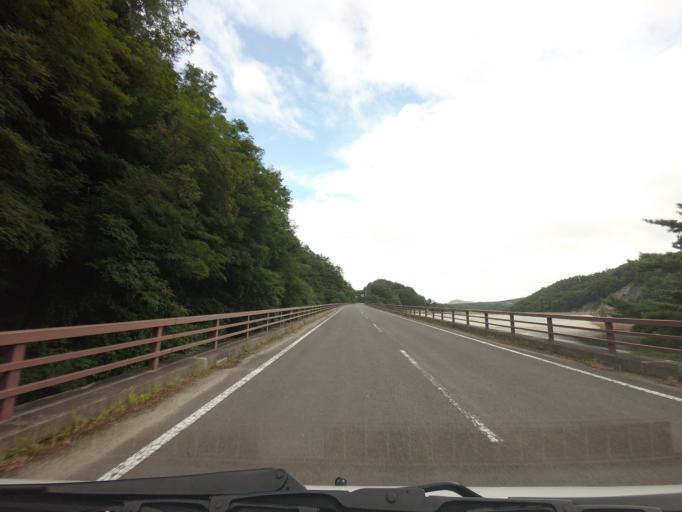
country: JP
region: Fukushima
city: Motomiya
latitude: 37.5471
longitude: 140.3056
